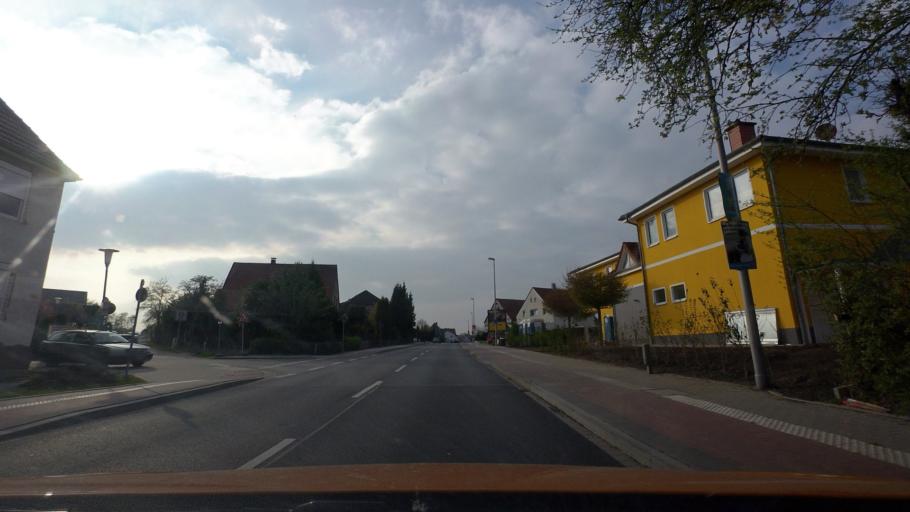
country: DE
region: North Rhine-Westphalia
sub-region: Regierungsbezirk Detmold
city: Herford
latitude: 52.1244
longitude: 8.6347
